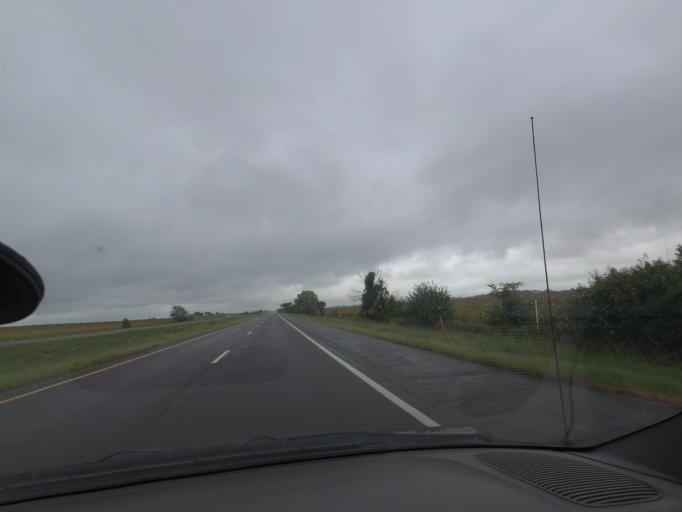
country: US
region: Illinois
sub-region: Champaign County
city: Mahomet
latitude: 40.1203
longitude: -88.4600
